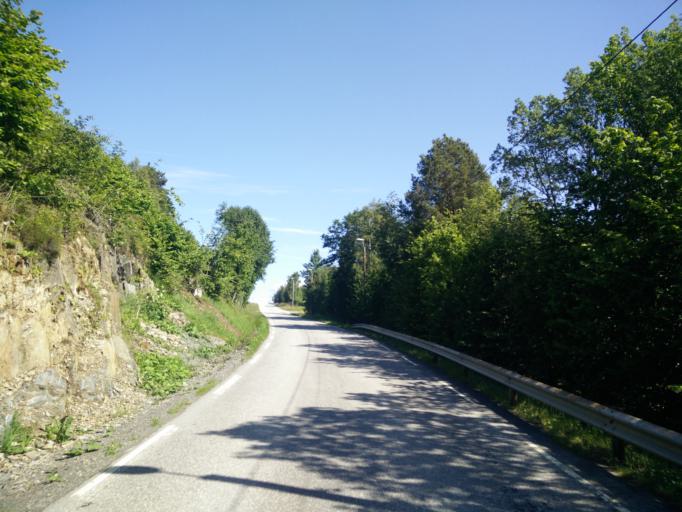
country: NO
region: More og Romsdal
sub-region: Kristiansund
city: Rensvik
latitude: 63.0507
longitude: 7.8620
